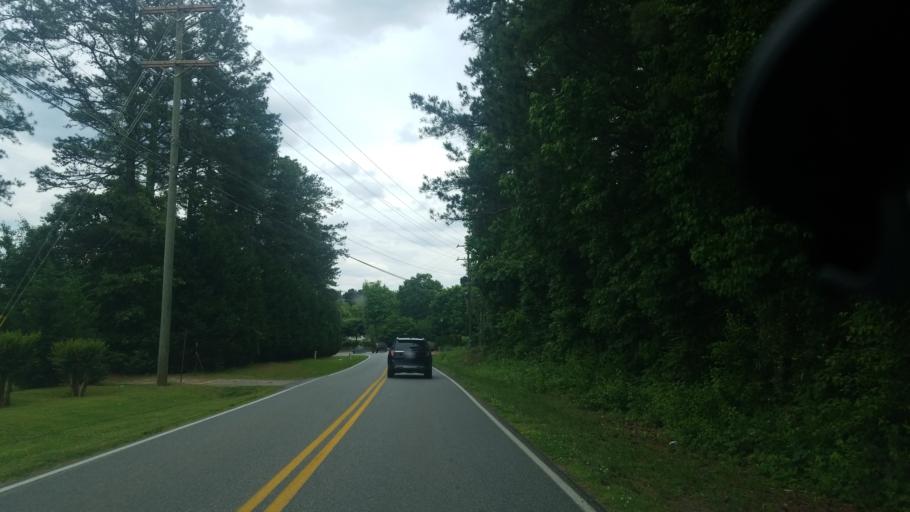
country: US
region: Georgia
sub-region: Forsyth County
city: Cumming
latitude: 34.1690
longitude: -84.1259
